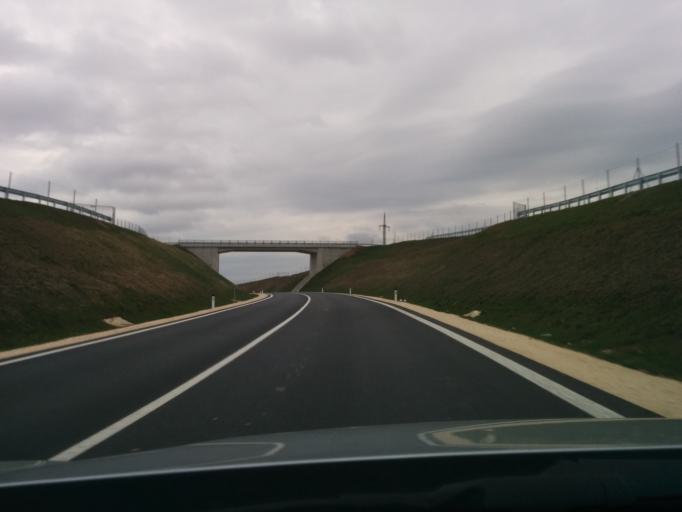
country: AT
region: Lower Austria
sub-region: Politischer Bezirk Mistelbach
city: Mistelbach
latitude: 48.5836
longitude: 16.5550
